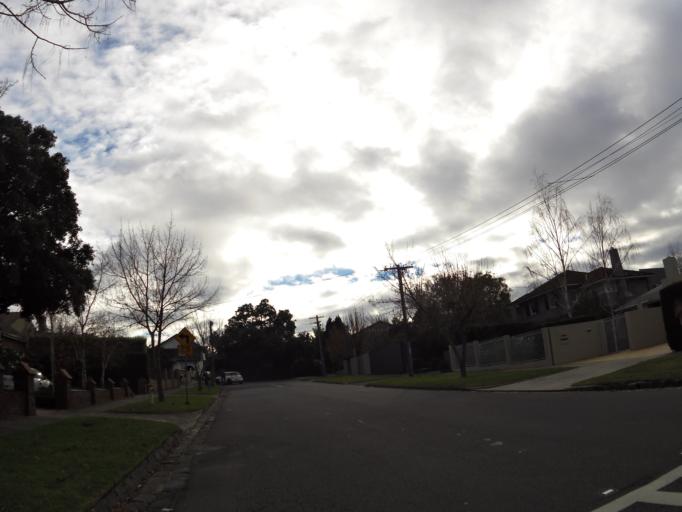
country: AU
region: Victoria
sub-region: Boroondara
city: Kew
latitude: -37.8115
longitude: 145.0204
